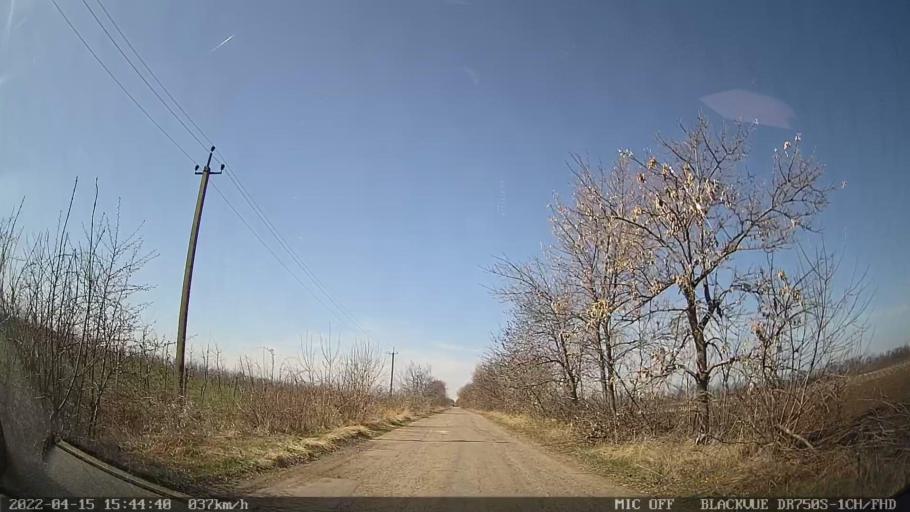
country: MD
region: Raionul Ocnita
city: Otaci
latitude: 48.3715
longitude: 27.9216
